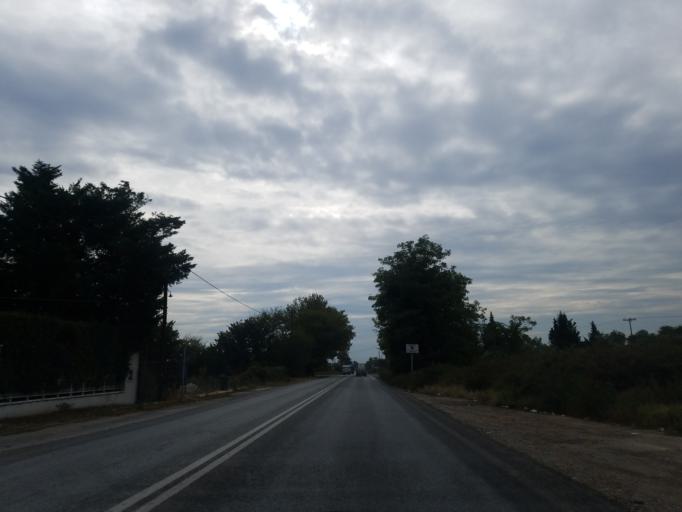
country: GR
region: Thessaly
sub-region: Trikala
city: Kalampaka
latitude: 39.6949
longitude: 21.6413
